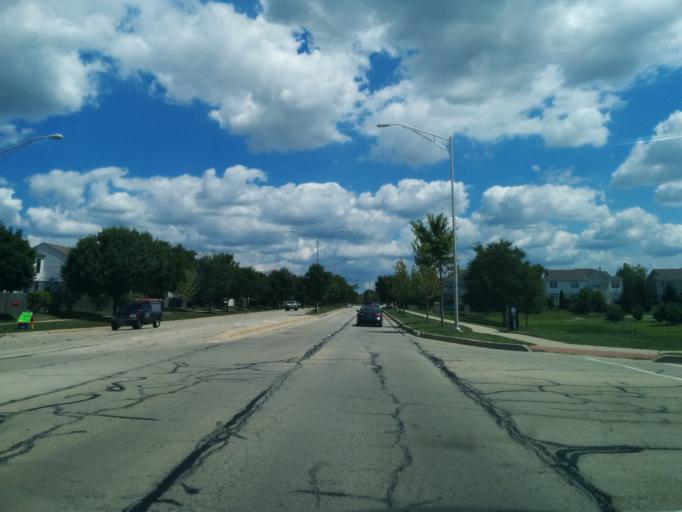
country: US
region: Illinois
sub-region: Will County
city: Romeoville
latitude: 41.6821
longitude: -88.1371
